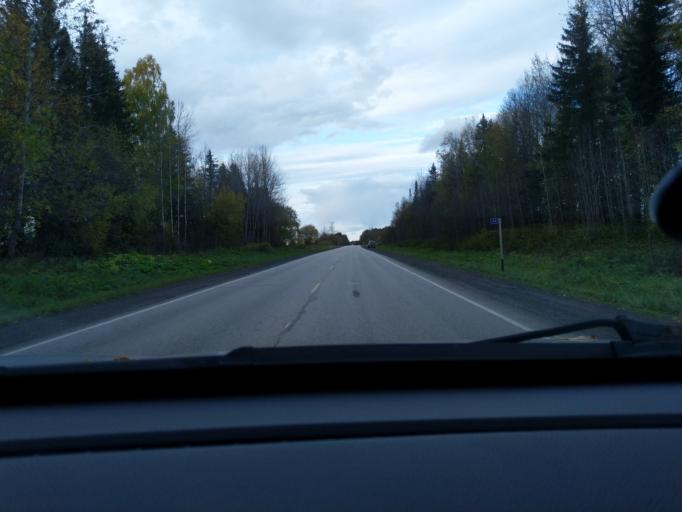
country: RU
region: Perm
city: Dobryanka
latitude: 58.3806
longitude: 56.4916
